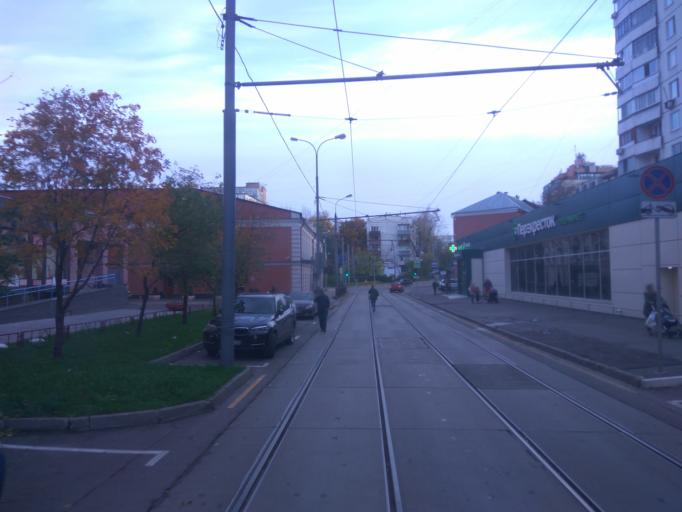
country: RU
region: Moscow
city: Mar'ina Roshcha
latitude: 55.7861
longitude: 37.6014
